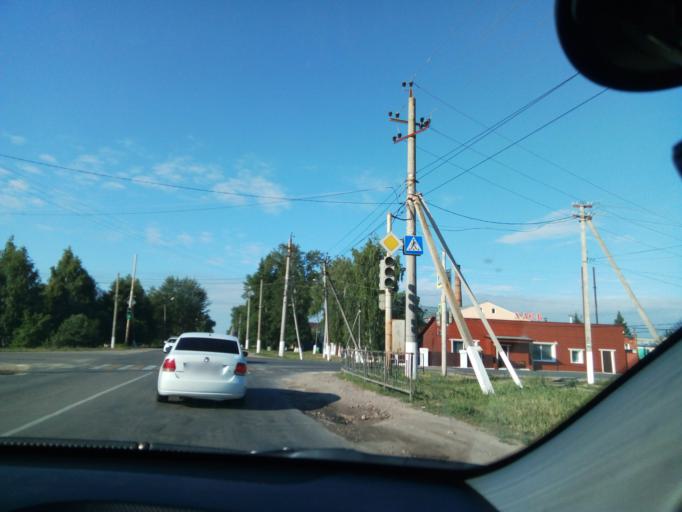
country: RU
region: Rjazan
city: Sasovo
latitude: 54.3503
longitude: 41.9241
